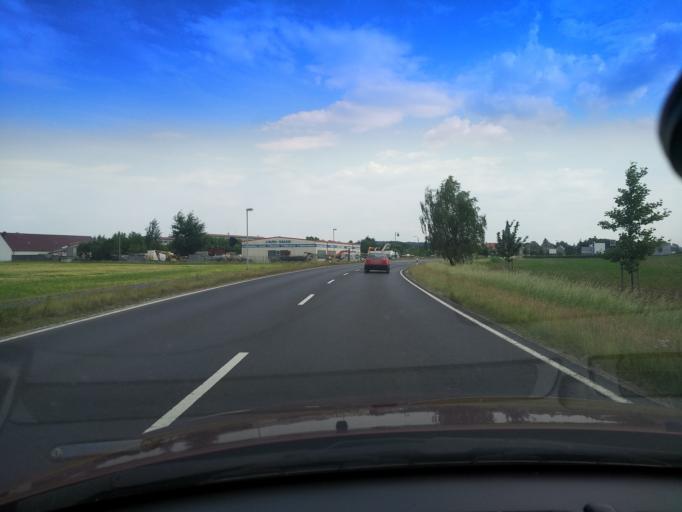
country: DE
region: Saxony
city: Kodersdorf
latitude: 51.2360
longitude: 14.8903
